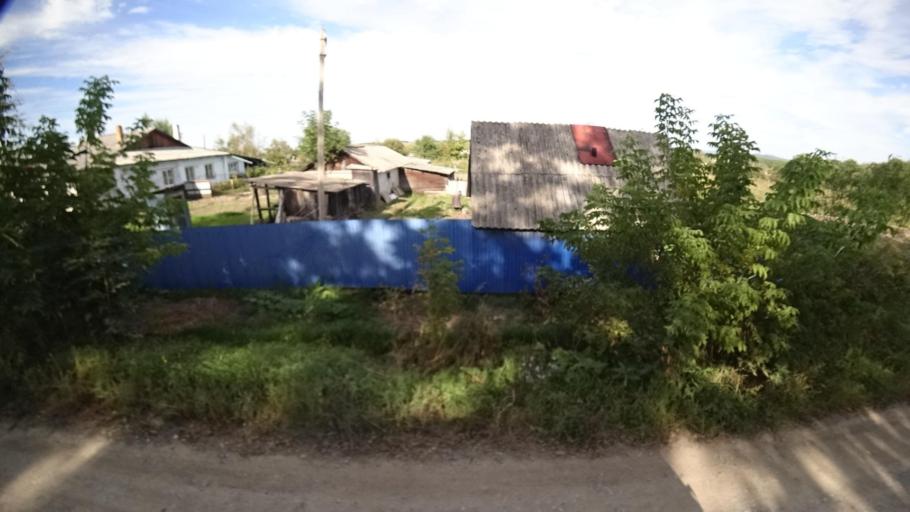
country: RU
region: Primorskiy
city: Dostoyevka
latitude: 44.3055
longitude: 133.4534
